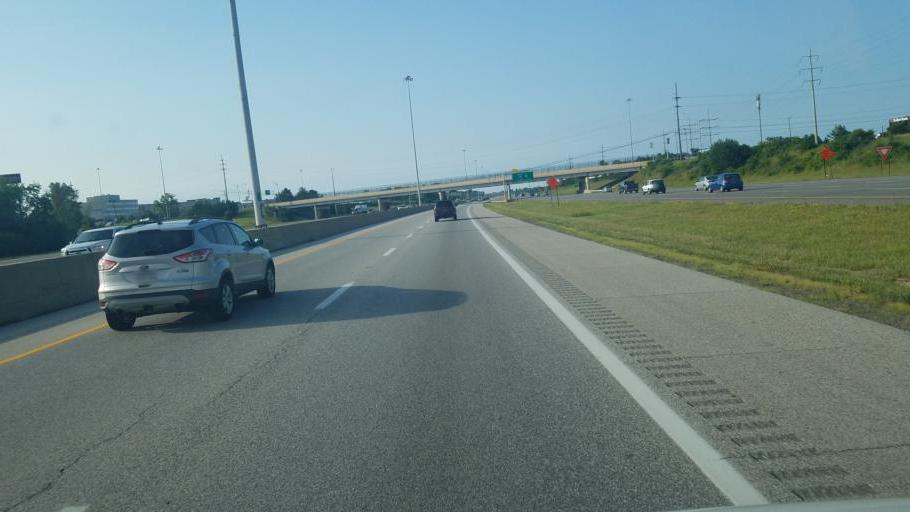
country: US
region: Ohio
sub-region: Cuyahoga County
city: Orange
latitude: 41.4610
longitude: -81.4912
